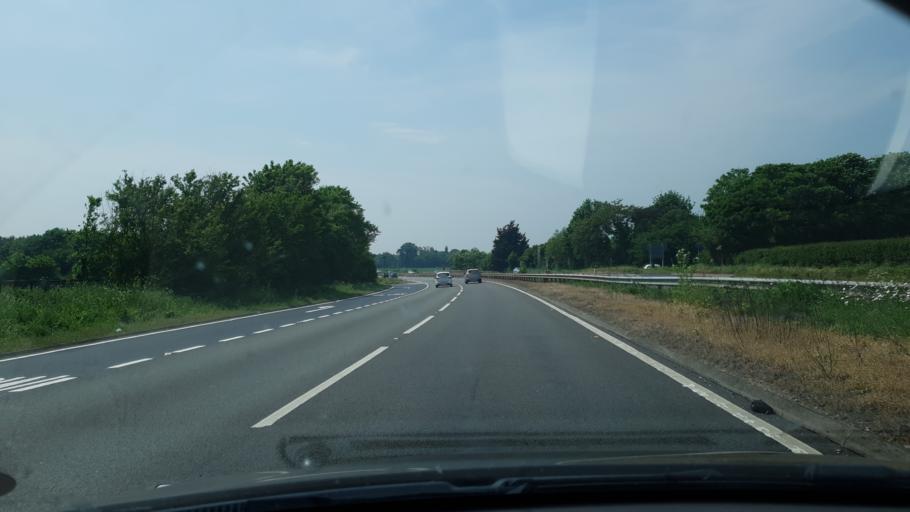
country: GB
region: England
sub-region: Suffolk
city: East Bergholt
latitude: 51.9875
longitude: 1.0105
